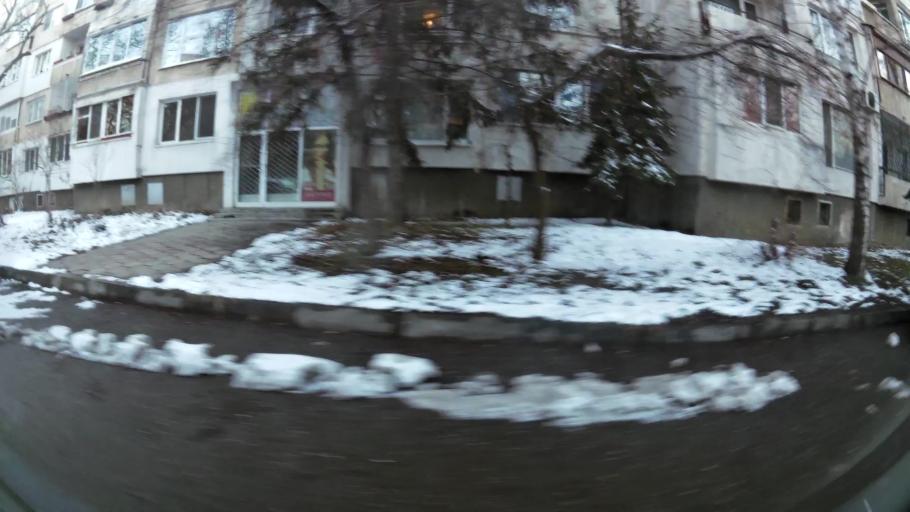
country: BG
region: Sofia-Capital
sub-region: Stolichna Obshtina
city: Sofia
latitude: 42.6824
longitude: 23.3747
